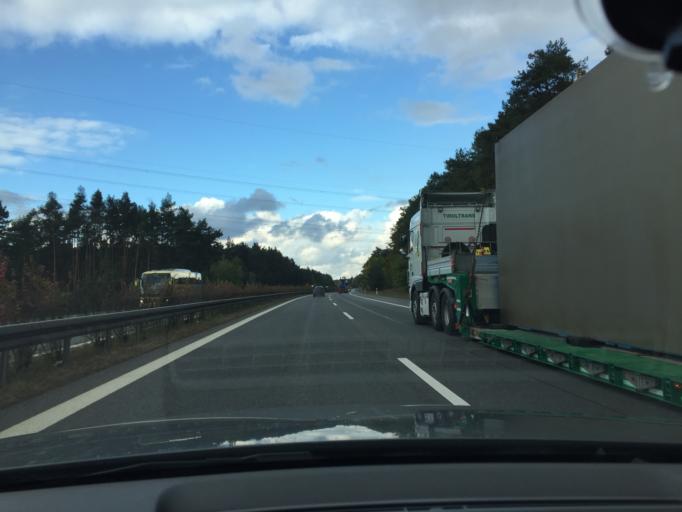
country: DE
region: Brandenburg
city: Bronkow
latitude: 51.6342
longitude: 13.9411
